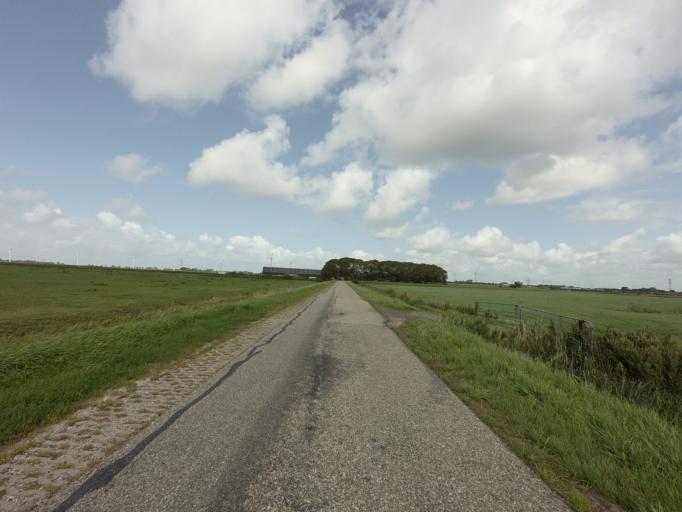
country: NL
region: Friesland
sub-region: Gemeente Franekeradeel
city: Sexbierum
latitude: 53.1709
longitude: 5.4889
